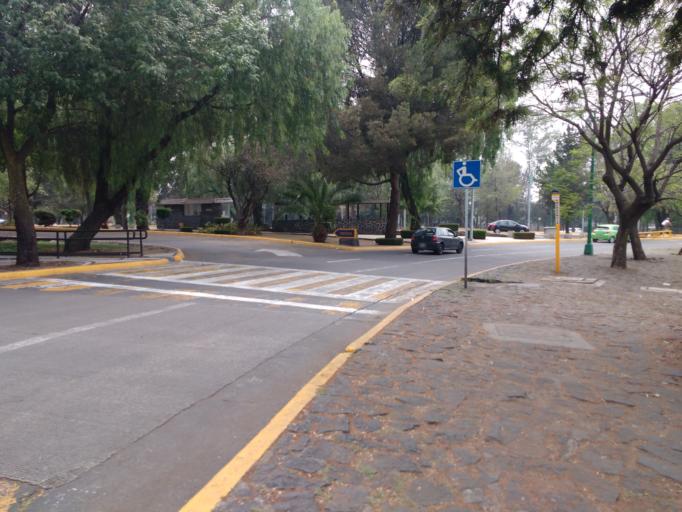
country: MX
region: Mexico City
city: Magdalena Contreras
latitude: 19.3304
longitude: -99.1885
